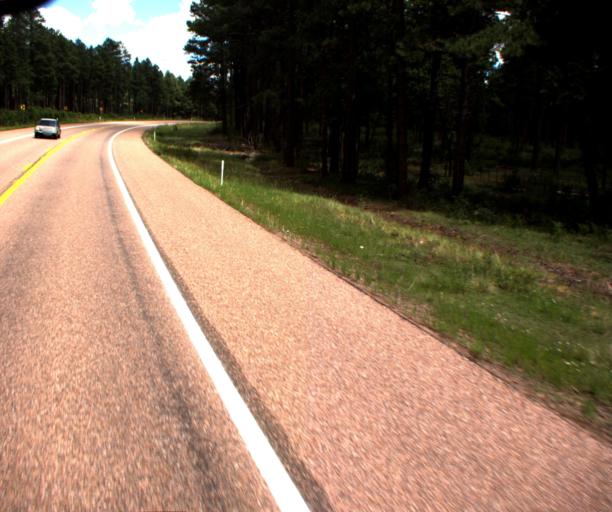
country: US
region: Arizona
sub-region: Navajo County
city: Pinetop-Lakeside
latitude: 34.0789
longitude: -109.8201
